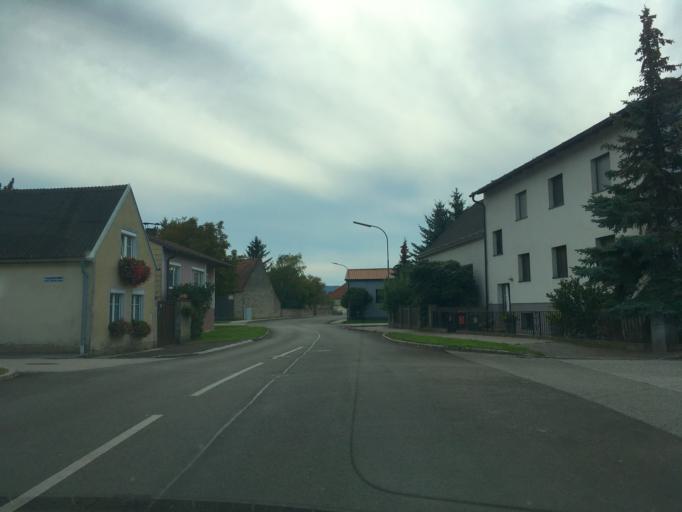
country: AT
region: Lower Austria
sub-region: Politischer Bezirk Bruck an der Leitha
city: Trautmannsdorf an der Leitha
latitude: 48.0223
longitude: 16.6778
